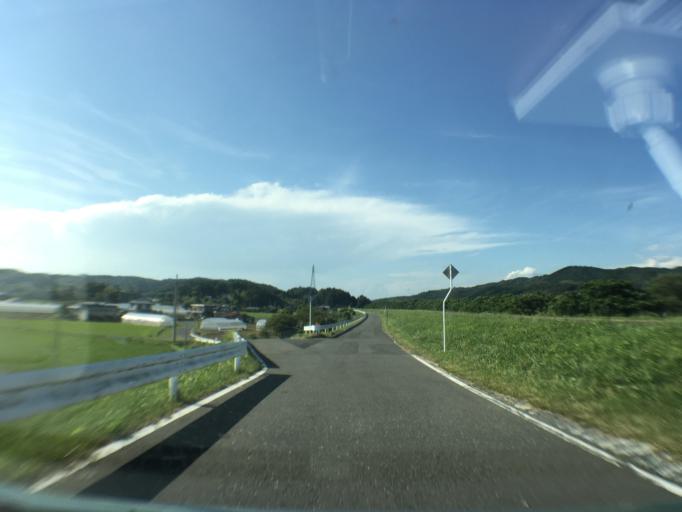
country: JP
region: Miyagi
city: Wakuya
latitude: 38.6134
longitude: 141.2938
